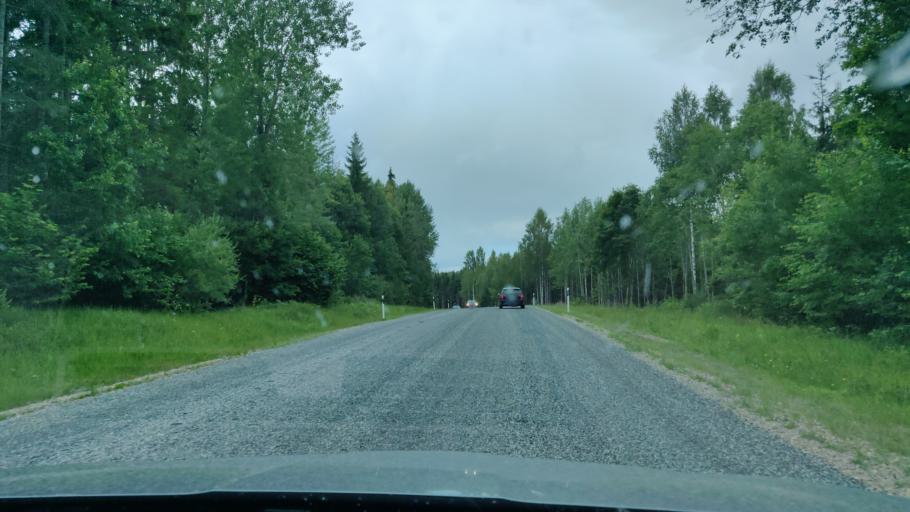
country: EE
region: Vorumaa
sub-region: Antsla vald
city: Vana-Antsla
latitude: 58.0269
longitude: 26.5775
